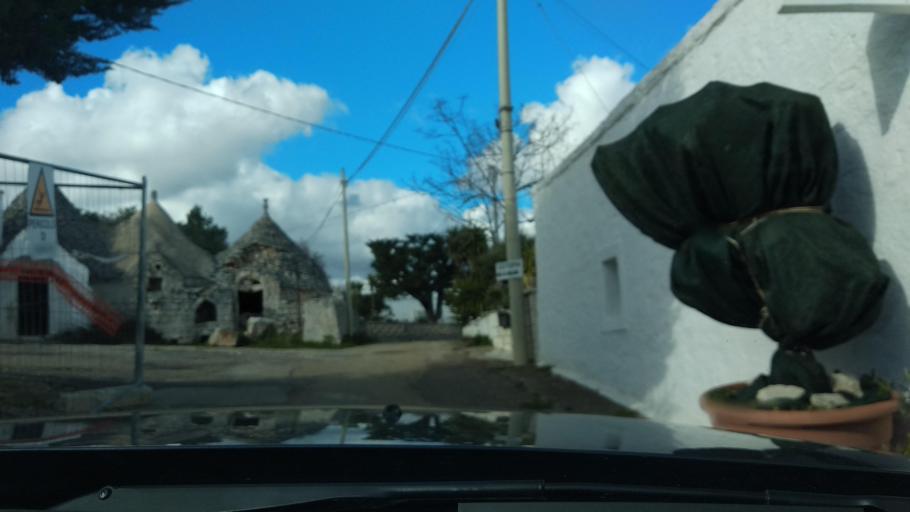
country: IT
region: Apulia
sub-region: Provincia di Brindisi
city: Casalini
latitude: 40.6961
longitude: 17.4699
